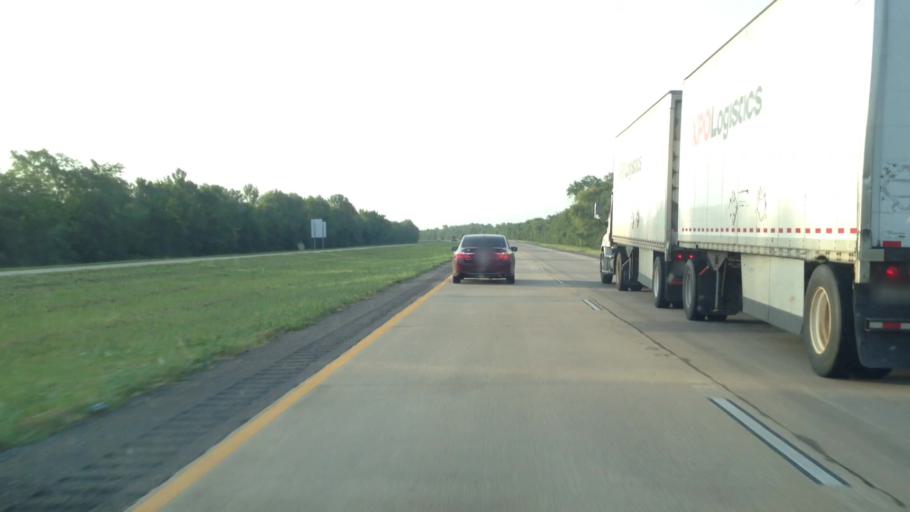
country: US
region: Louisiana
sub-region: Natchitoches Parish
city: Vienna Bend
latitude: 31.5817
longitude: -93.0253
